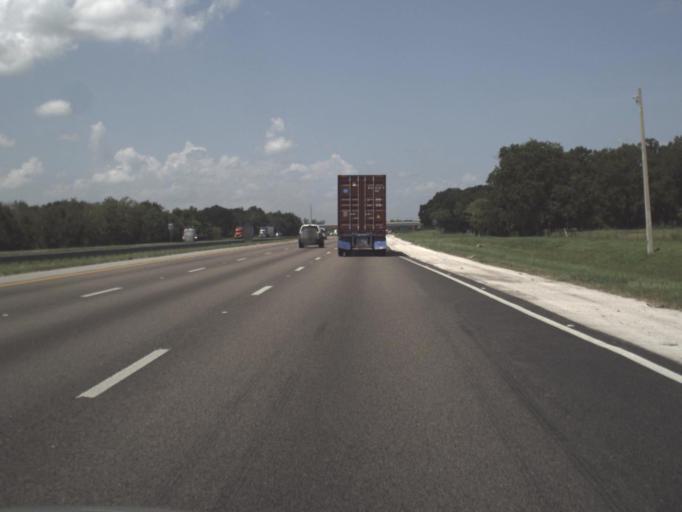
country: US
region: Florida
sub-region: Hillsborough County
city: Dover
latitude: 28.0273
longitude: -82.1953
